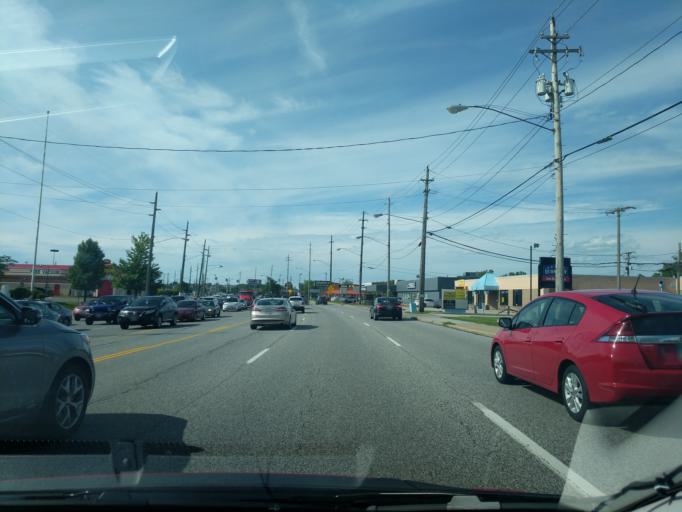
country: US
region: Ohio
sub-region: Cuyahoga County
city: North Randall
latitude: 41.4289
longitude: -81.5253
